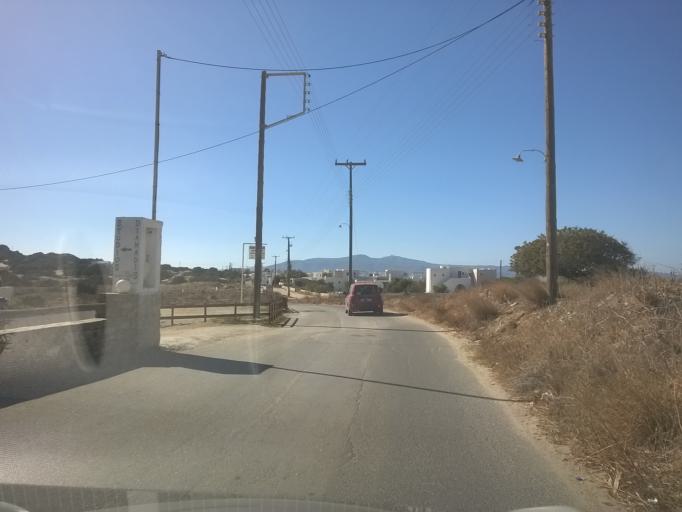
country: GR
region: South Aegean
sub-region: Nomos Kykladon
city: Naxos
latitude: 37.0257
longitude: 25.3739
